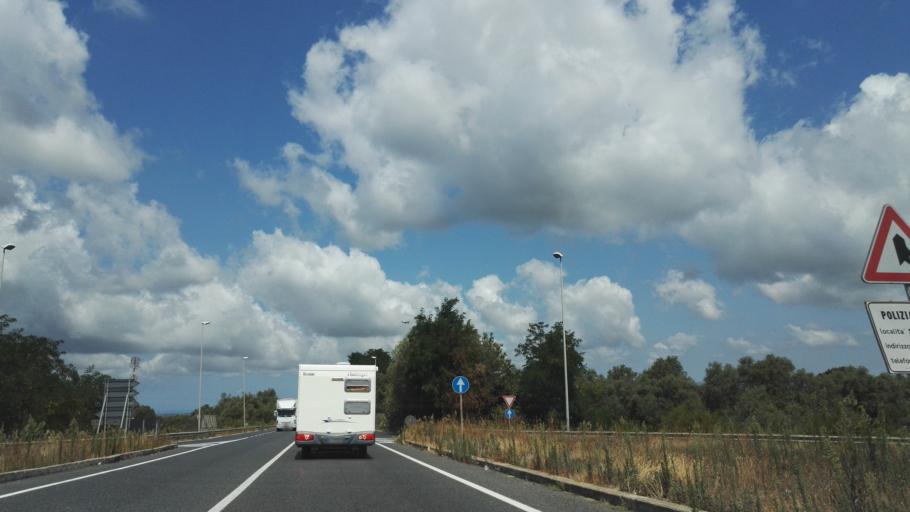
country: IT
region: Calabria
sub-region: Provincia di Reggio Calabria
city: Melicucco
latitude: 38.4291
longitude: 16.0554
